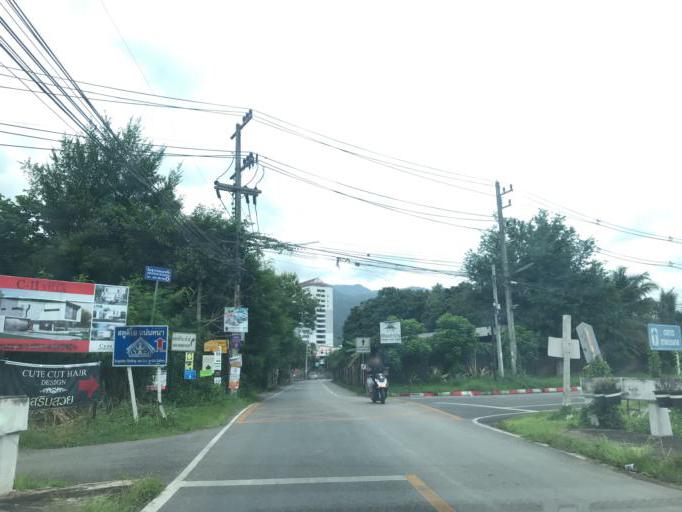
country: TH
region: Chiang Mai
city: Chiang Mai
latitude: 18.8163
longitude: 98.9629
